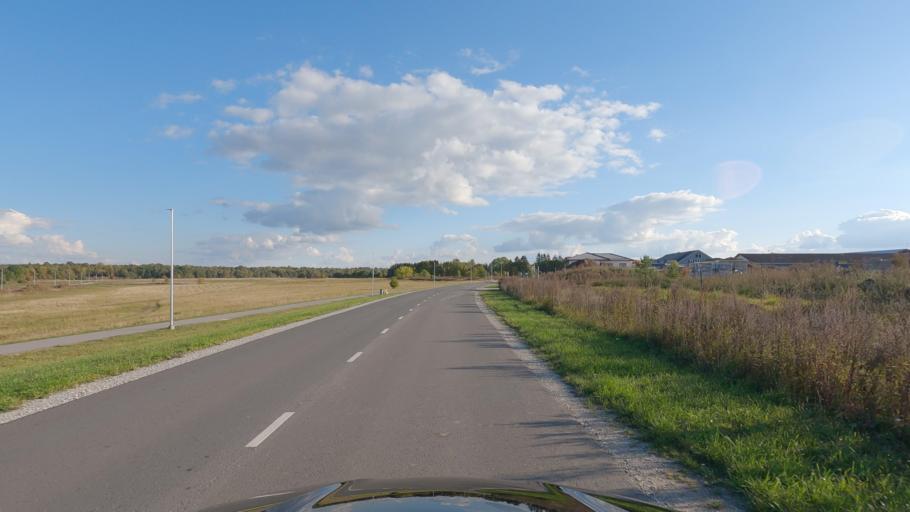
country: EE
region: Harju
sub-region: Saue vald
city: Laagri
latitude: 59.3407
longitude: 24.6508
